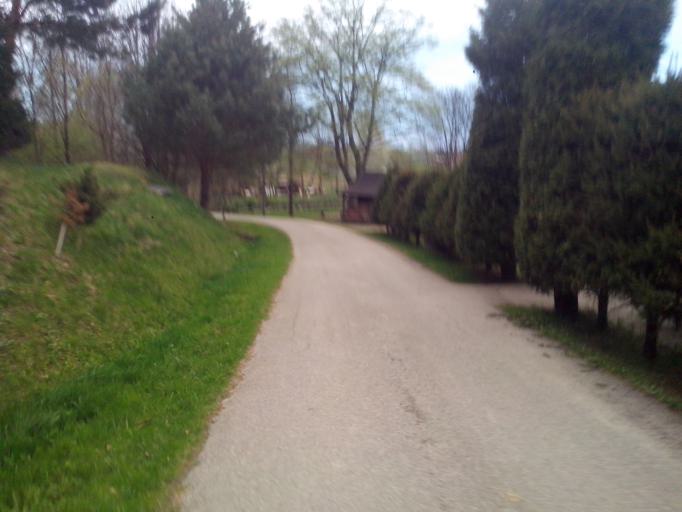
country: PL
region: Subcarpathian Voivodeship
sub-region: Powiat strzyzowski
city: Strzyzow
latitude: 49.8374
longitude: 21.8035
